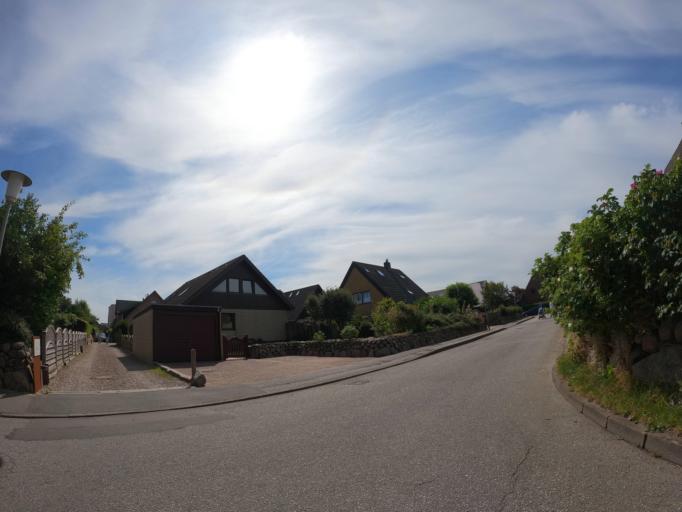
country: DE
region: Schleswig-Holstein
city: Westerland
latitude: 54.9251
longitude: 8.3190
